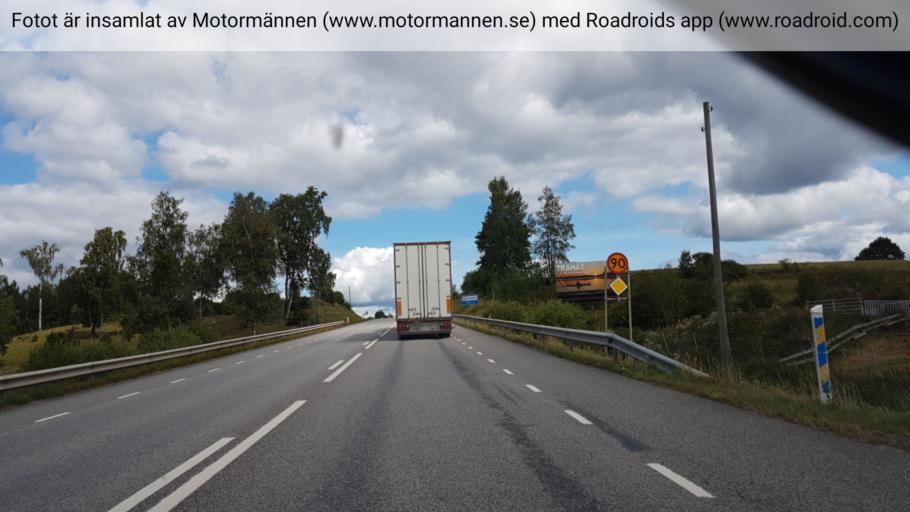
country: SE
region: Joenkoeping
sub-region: Tranas Kommun
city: Tranas
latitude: 58.0078
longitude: 14.9284
